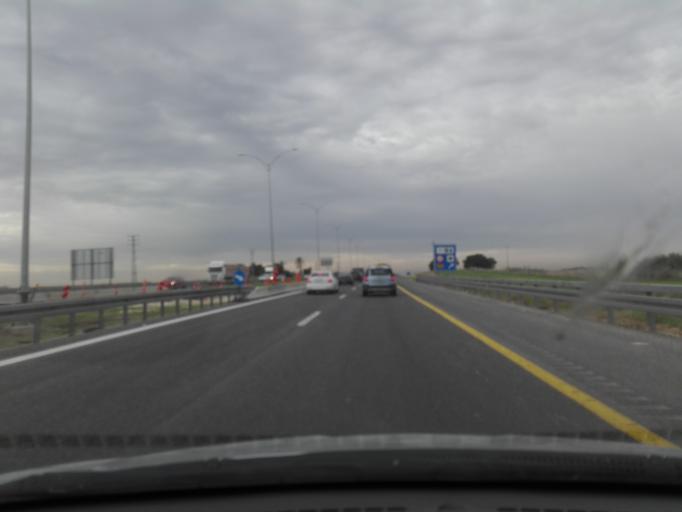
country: IL
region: Central District
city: Ramla
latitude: 31.8892
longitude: 34.8812
